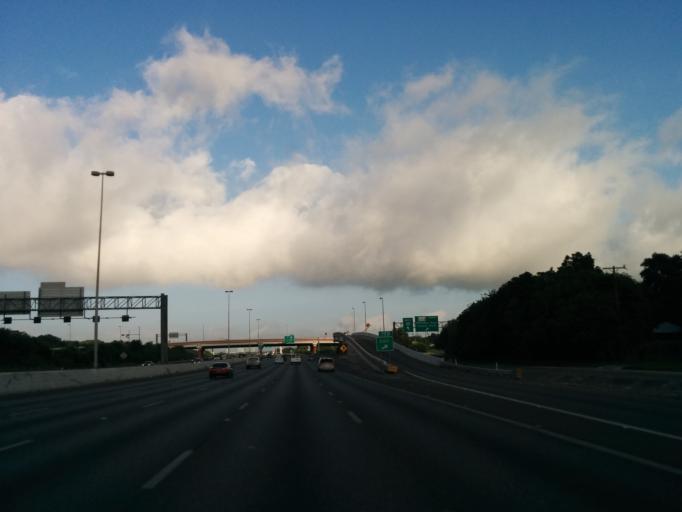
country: US
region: Texas
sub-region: Bexar County
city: Castle Hills
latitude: 29.5208
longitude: -98.5092
